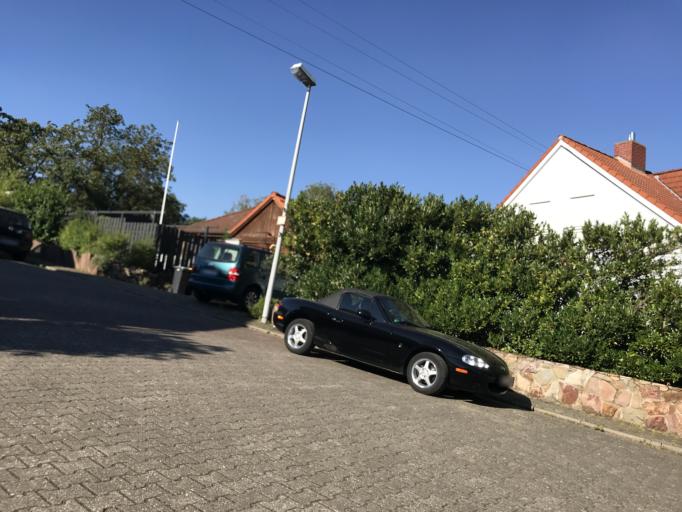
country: DE
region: Rheinland-Pfalz
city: Stadecken-Elsheim
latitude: 49.9211
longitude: 8.1231
